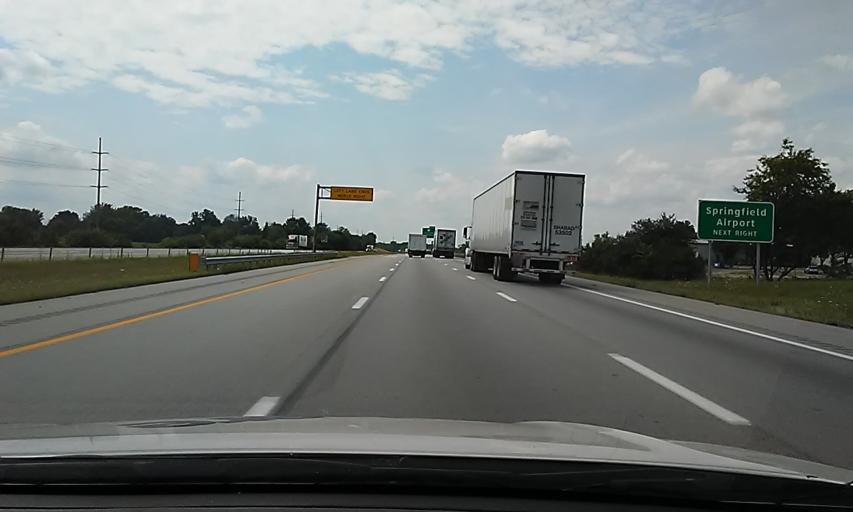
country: US
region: Ohio
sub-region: Clark County
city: Springfield
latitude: 39.8908
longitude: -83.7957
